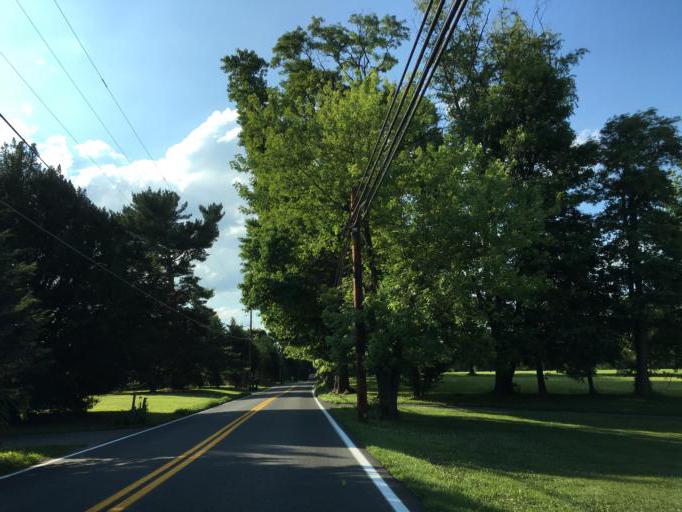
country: US
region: Maryland
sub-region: Baltimore County
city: Kingsville
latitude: 39.4784
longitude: -76.4505
